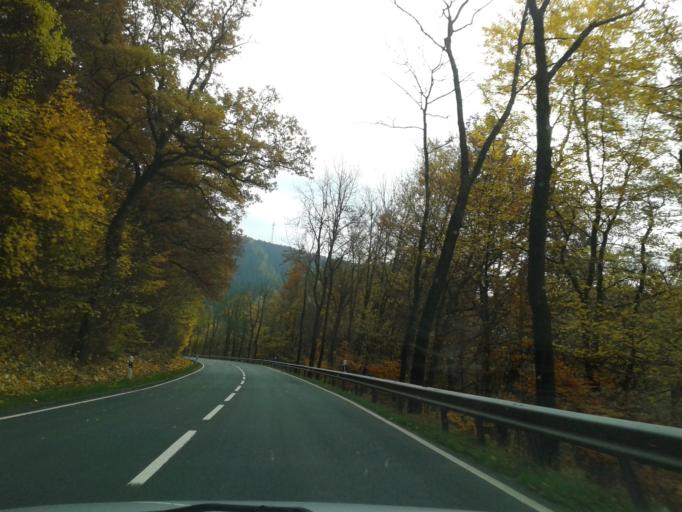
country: DE
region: North Rhine-Westphalia
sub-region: Regierungsbezirk Arnsberg
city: Bad Laasphe
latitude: 50.9527
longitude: 8.3582
